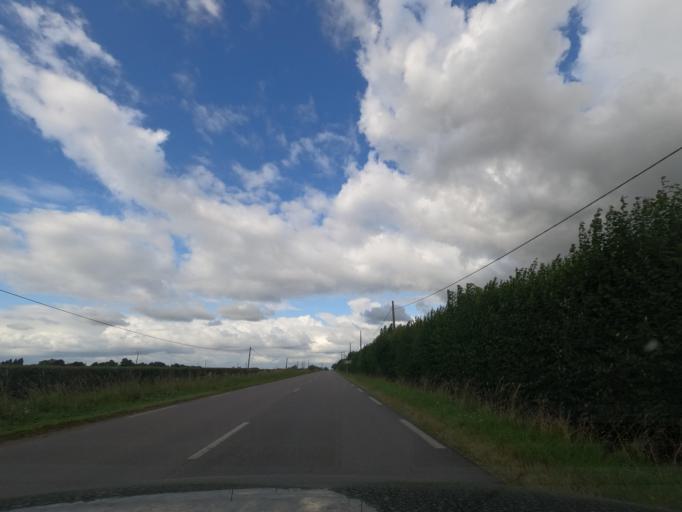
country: FR
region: Haute-Normandie
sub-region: Departement de l'Eure
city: Broglie
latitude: 48.9617
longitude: 0.4727
